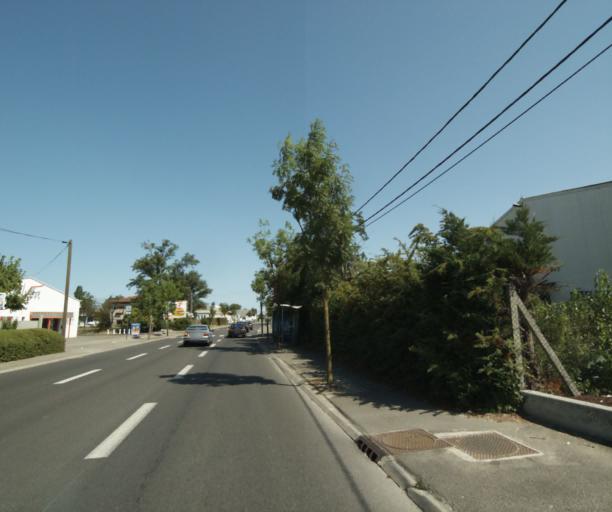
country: FR
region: Midi-Pyrenees
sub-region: Departement du Tarn-et-Garonne
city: Montauban
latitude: 44.0368
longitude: 1.3674
